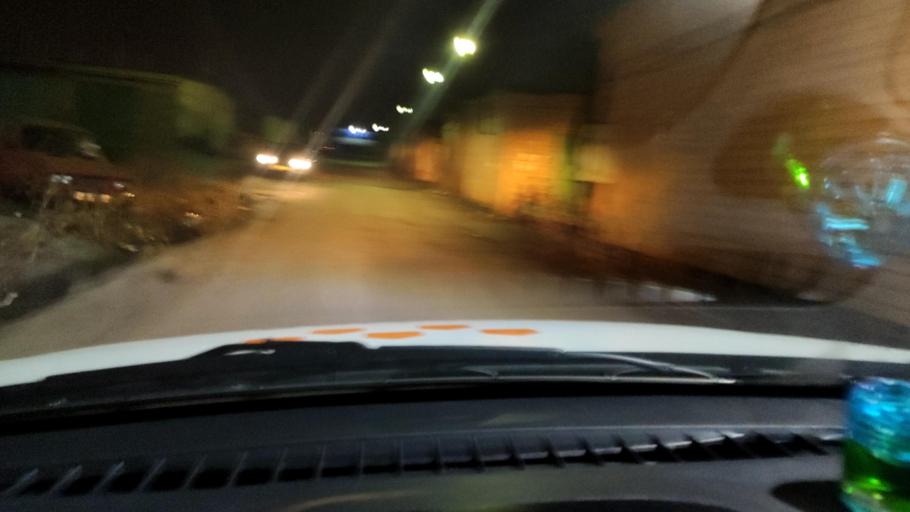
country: RU
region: Voronezj
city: Voronezh
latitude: 51.6361
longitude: 39.1288
